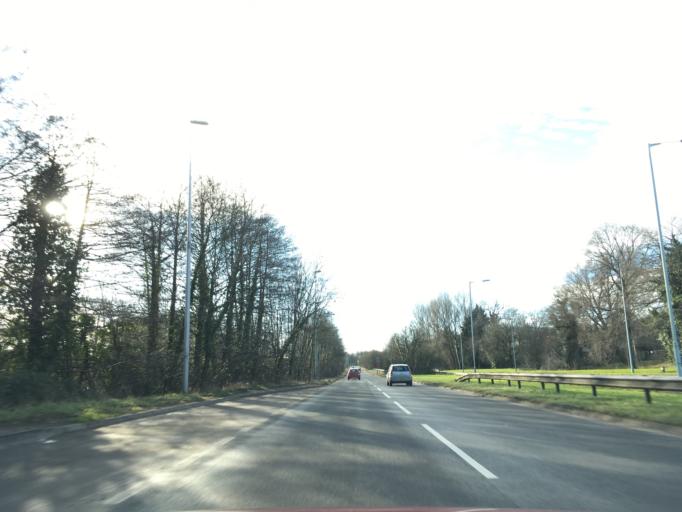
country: GB
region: Wales
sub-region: Torfaen County Borough
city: New Inn
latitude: 51.7100
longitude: -3.0032
